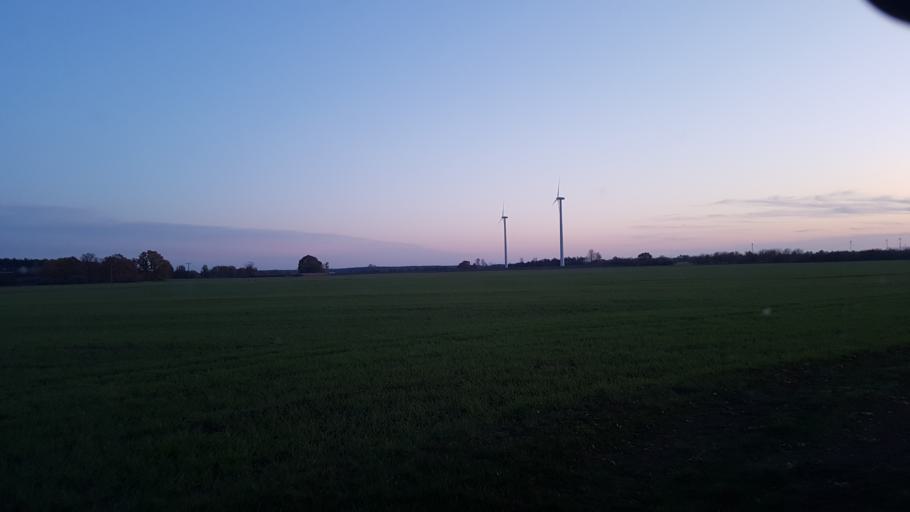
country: DE
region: Brandenburg
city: Schilda
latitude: 51.6344
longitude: 13.3407
